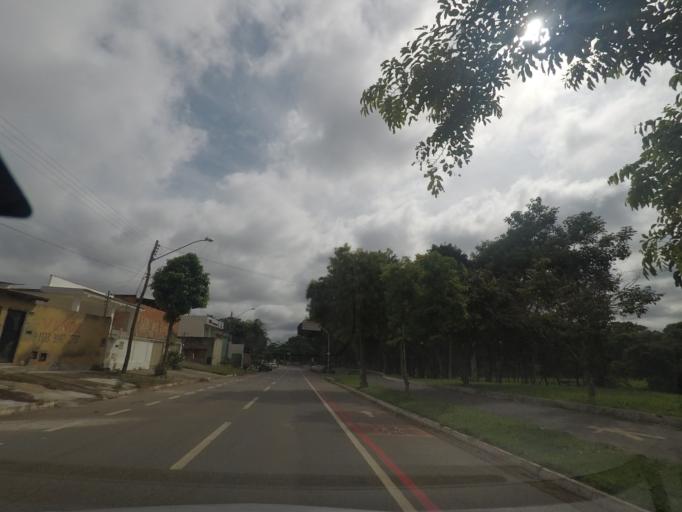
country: BR
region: Goias
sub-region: Goiania
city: Goiania
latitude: -16.7223
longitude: -49.2516
